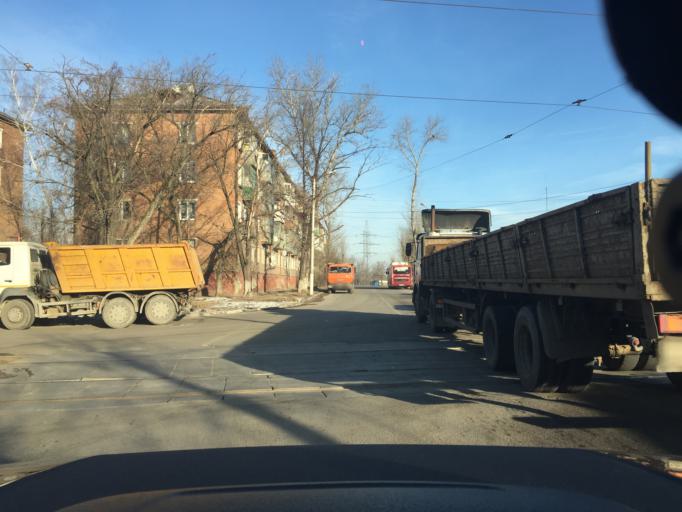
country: RU
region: Tula
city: Tula
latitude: 54.1778
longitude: 37.7097
